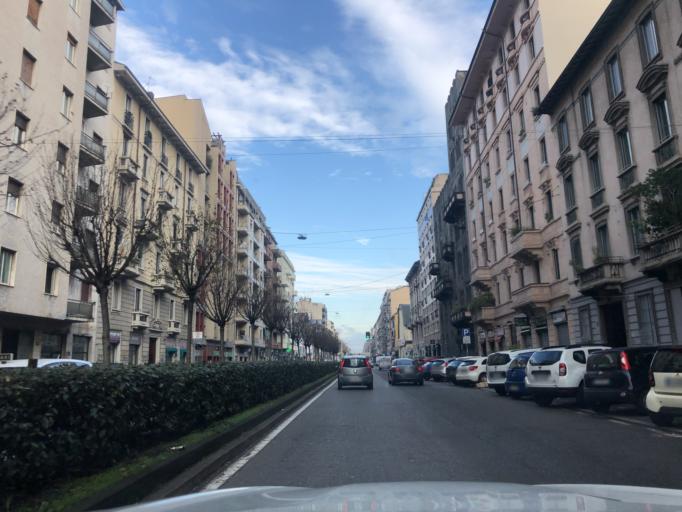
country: IT
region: Lombardy
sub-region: Citta metropolitana di Milano
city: Milano
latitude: 45.4919
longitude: 9.2185
